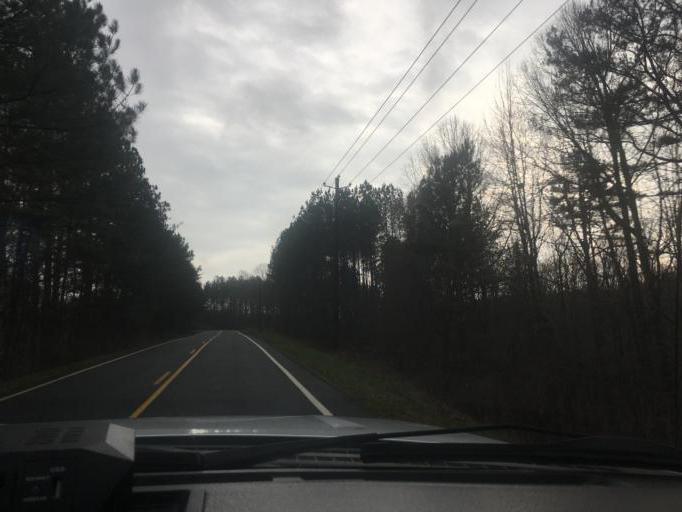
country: US
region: Georgia
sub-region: Dawson County
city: Dawsonville
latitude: 34.3482
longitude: -84.2062
